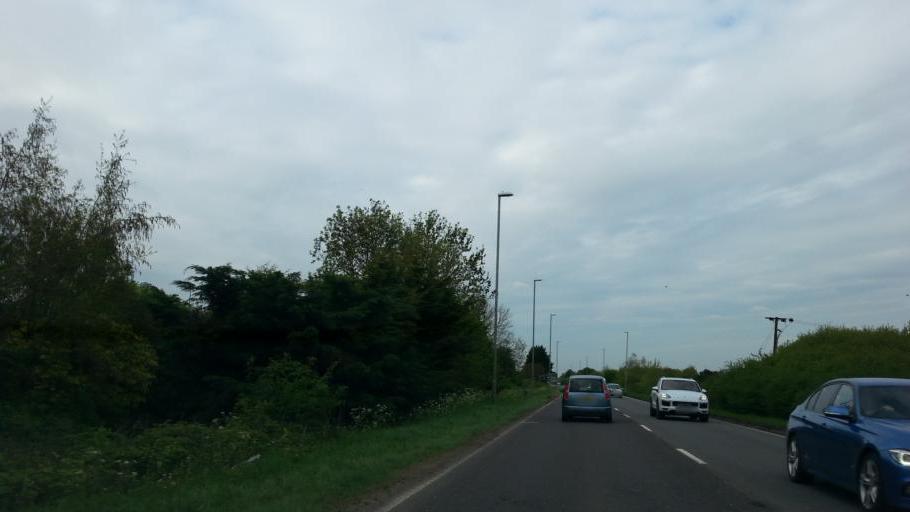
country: GB
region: England
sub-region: Cambridgeshire
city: Doddington
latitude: 52.5102
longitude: 0.0874
